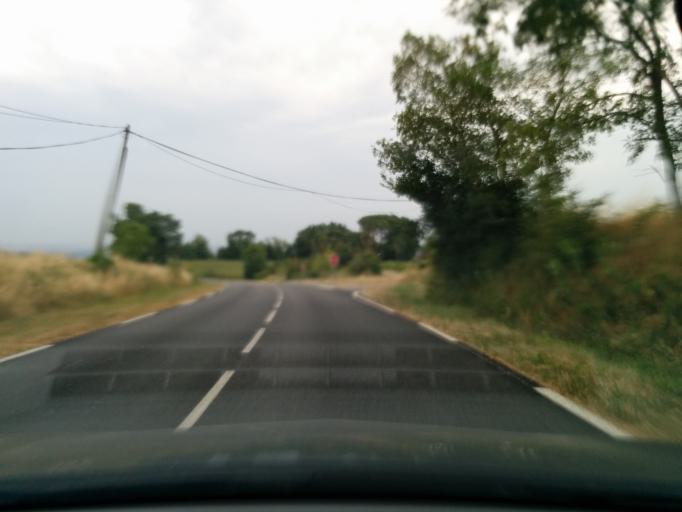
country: FR
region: Midi-Pyrenees
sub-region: Departement de la Haute-Garonne
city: Venerque
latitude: 43.4621
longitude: 1.4391
